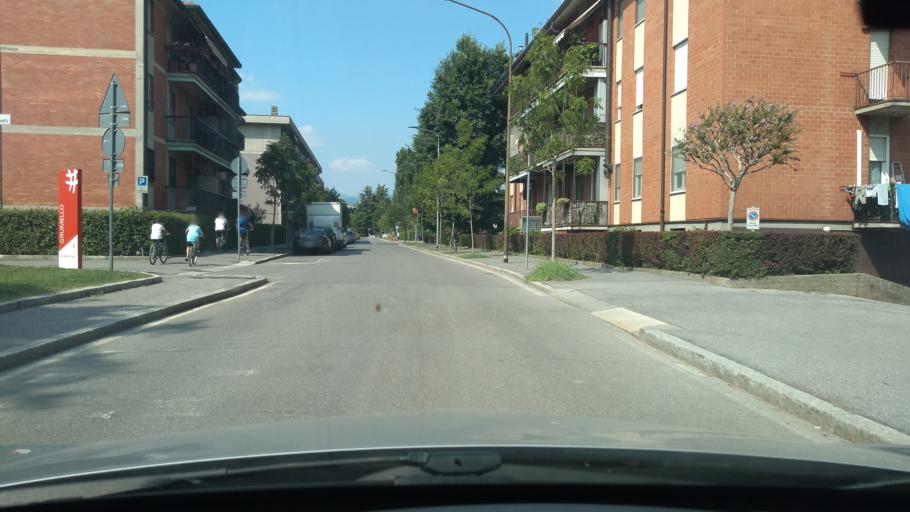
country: IT
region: Lombardy
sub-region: Provincia di Bergamo
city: Lallio
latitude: 45.6671
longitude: 9.6396
